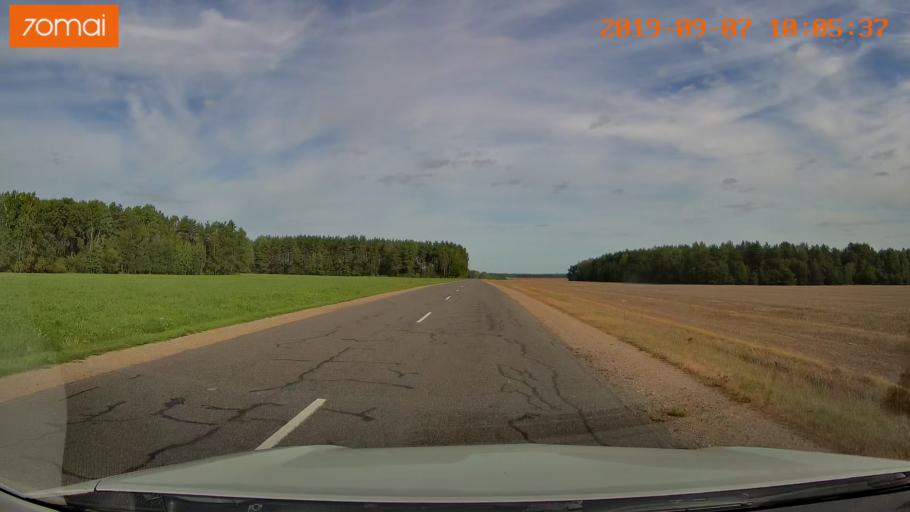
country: BY
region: Grodnenskaya
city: Voranava
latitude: 54.0499
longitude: 25.4065
